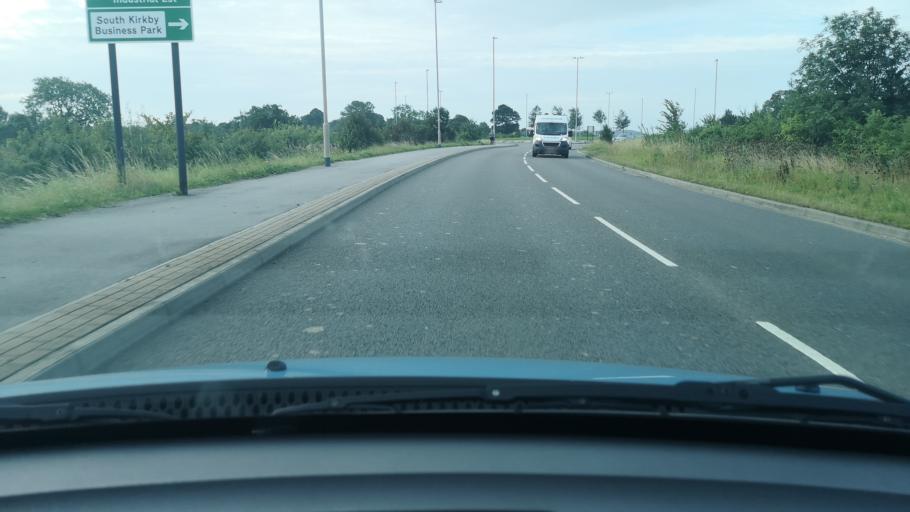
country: GB
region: England
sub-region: City and Borough of Wakefield
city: Upton
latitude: 53.6095
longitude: -1.2876
